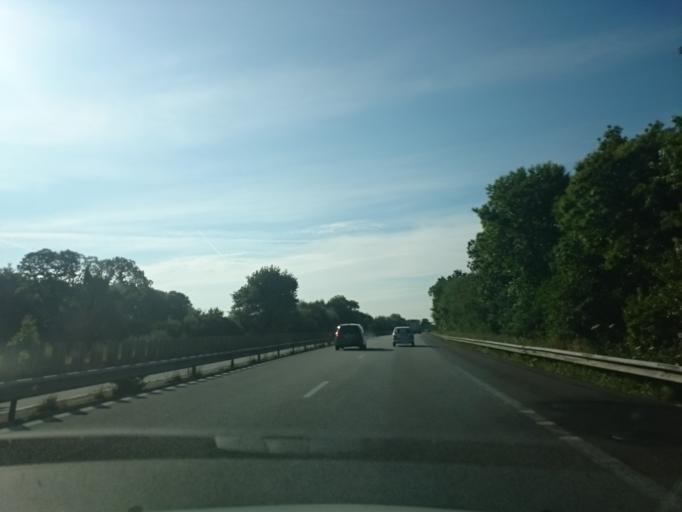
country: FR
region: Brittany
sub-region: Departement du Finistere
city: Saint-Yvi
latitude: 47.9309
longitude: -3.9035
